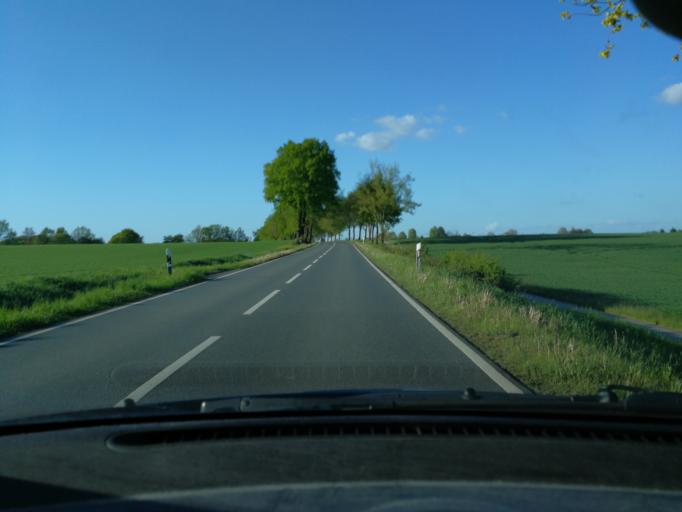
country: DE
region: Lower Saxony
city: Betzendorf
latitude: 53.1310
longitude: 10.3087
